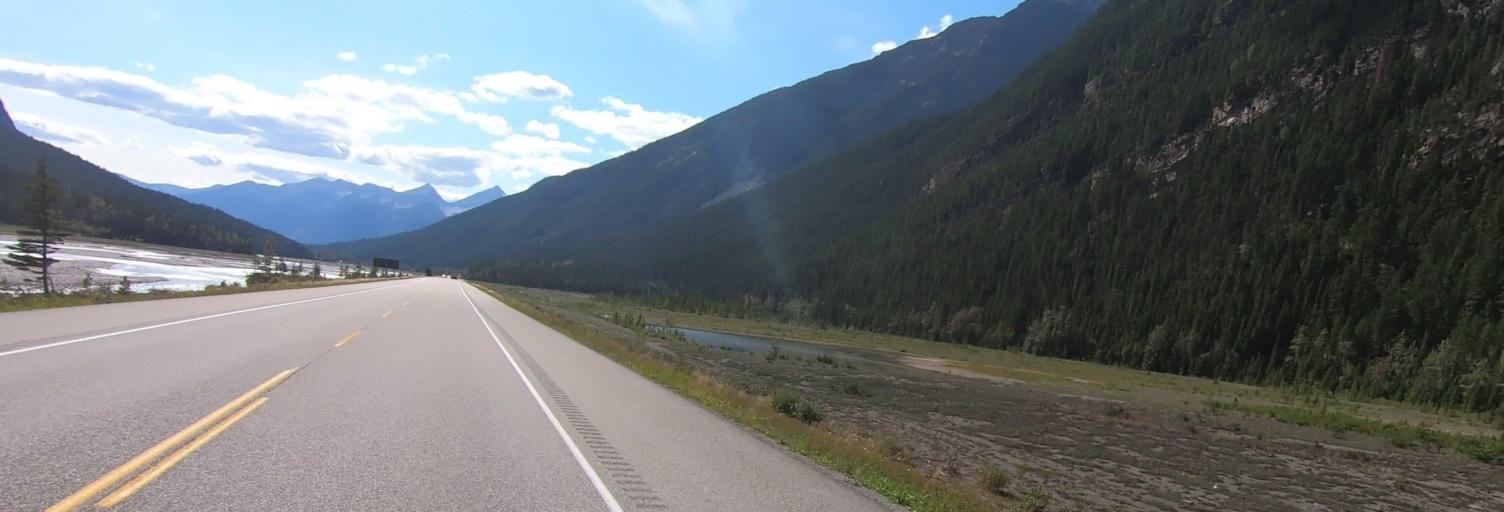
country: CA
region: Alberta
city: Lake Louise
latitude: 51.4136
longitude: -116.4555
